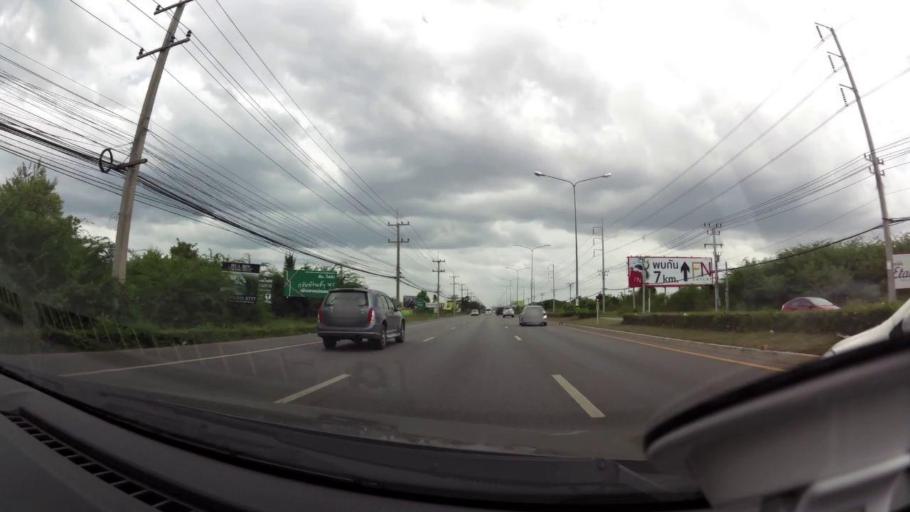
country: TH
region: Phetchaburi
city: Cha-am
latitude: 12.7423
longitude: 99.9593
